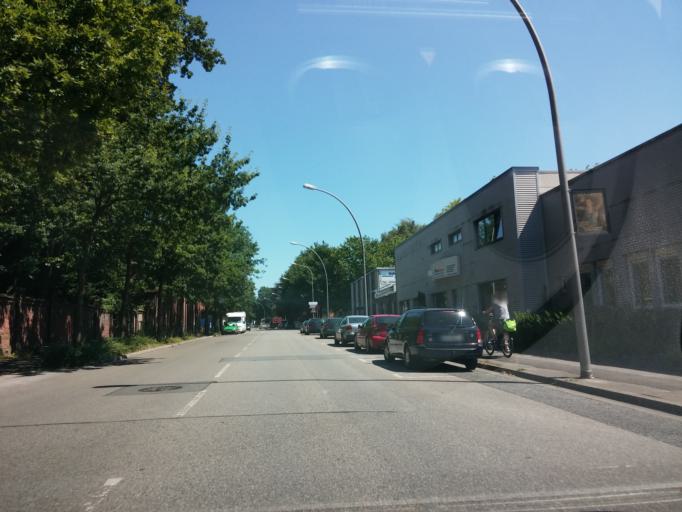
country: DE
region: North Rhine-Westphalia
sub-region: Regierungsbezirk Munster
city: Gladbeck
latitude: 51.5713
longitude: 6.9689
